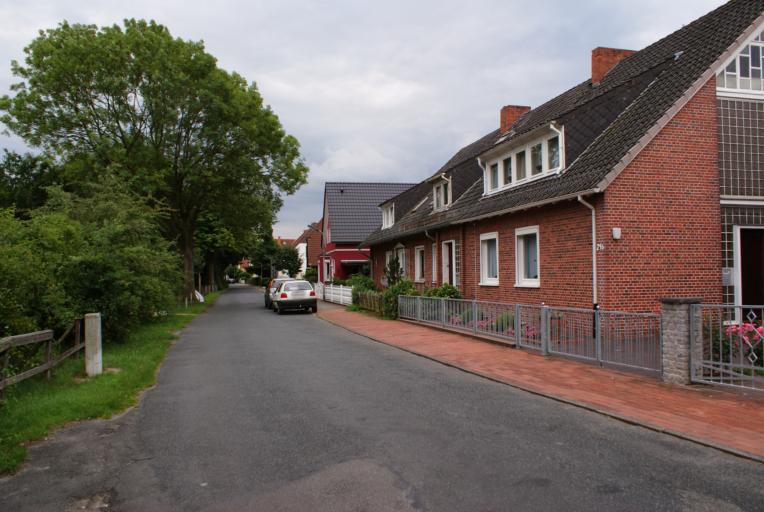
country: DE
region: Bremen
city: Bremen
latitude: 53.0950
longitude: 8.7507
